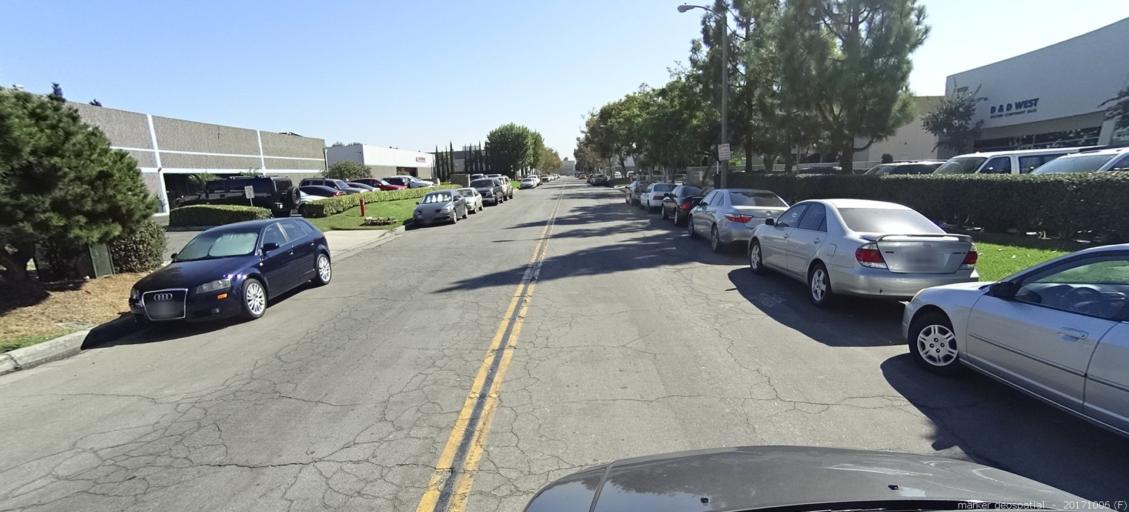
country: US
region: California
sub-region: Orange County
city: Stanton
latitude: 33.7983
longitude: -118.0105
